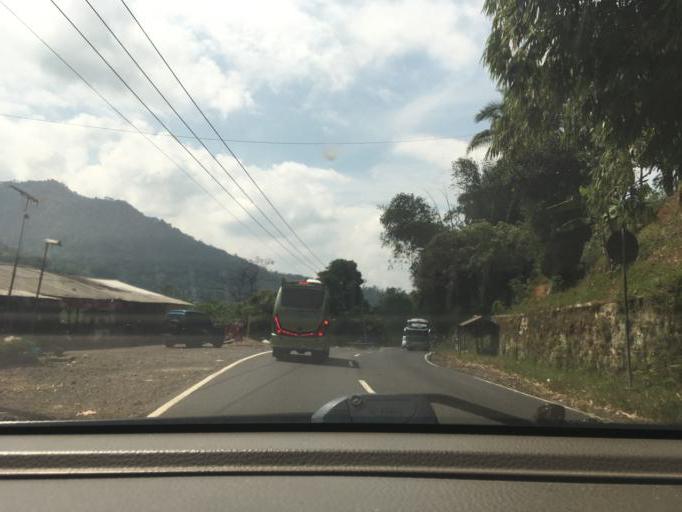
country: ID
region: West Java
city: Wage Cibahayu
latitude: -7.1164
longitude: 108.1198
